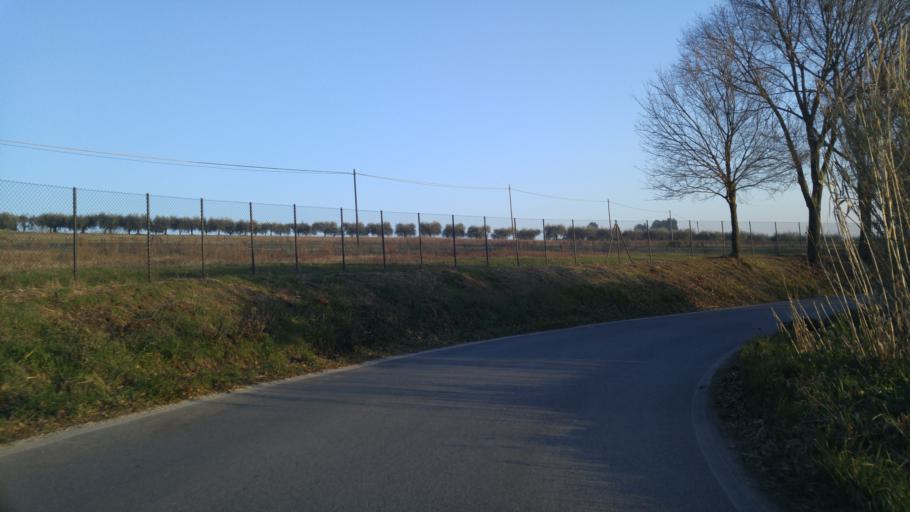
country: IT
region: The Marches
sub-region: Provincia di Pesaro e Urbino
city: Fenile
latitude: 43.8580
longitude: 12.9649
